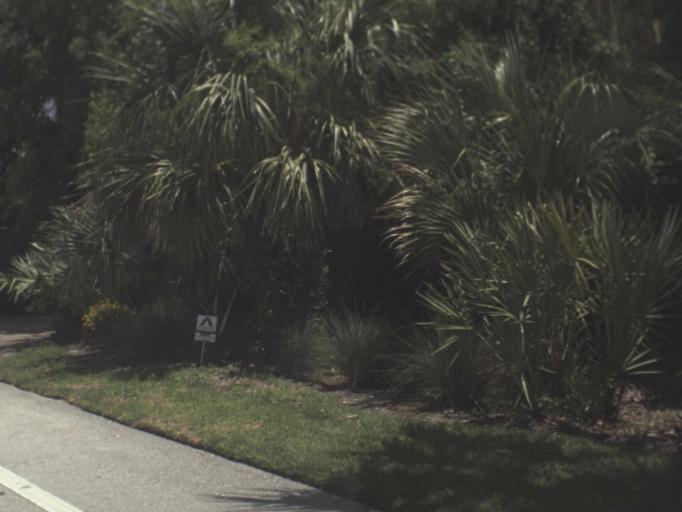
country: US
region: Florida
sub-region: Saint Johns County
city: Palm Valley
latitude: 30.1276
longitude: -81.3485
